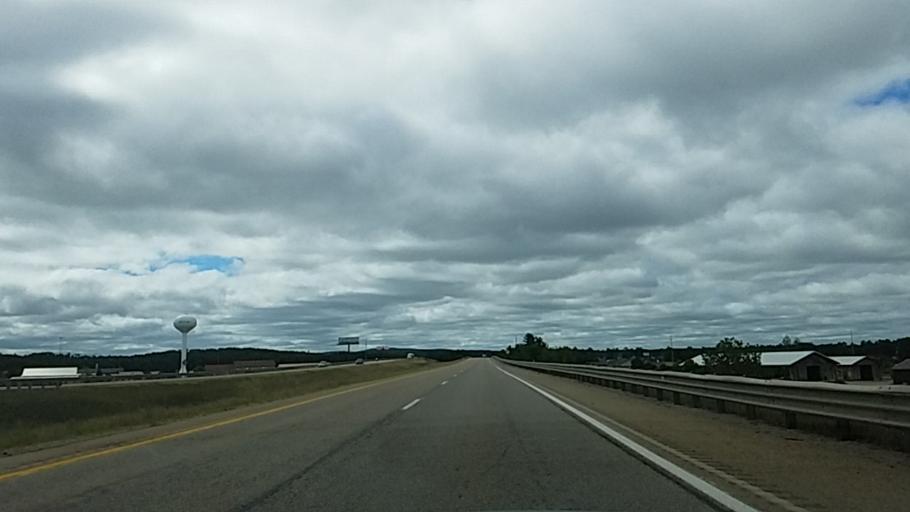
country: US
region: Michigan
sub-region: Crawford County
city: Grayling
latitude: 44.6559
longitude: -84.7008
